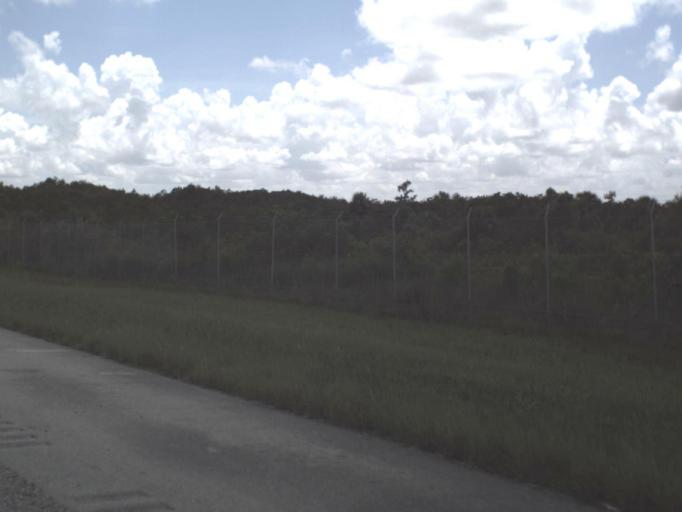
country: US
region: Florida
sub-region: Collier County
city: Immokalee
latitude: 26.1708
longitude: -80.9602
